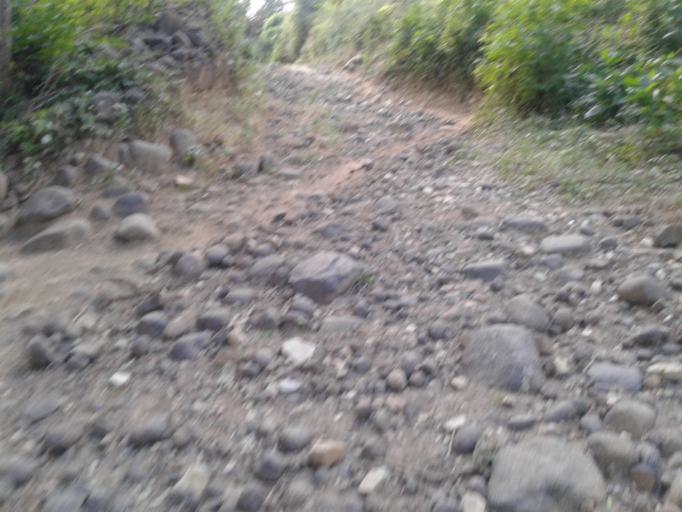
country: NI
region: Carazo
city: Santa Teresa
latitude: 11.6177
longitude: -86.1830
